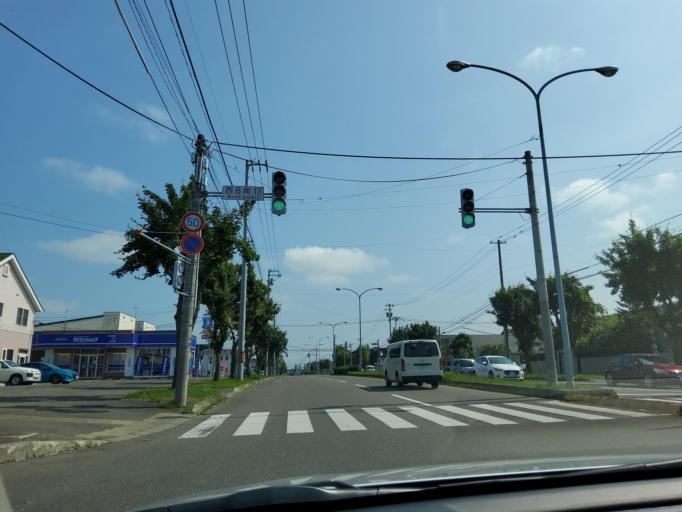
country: JP
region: Hokkaido
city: Obihiro
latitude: 42.9172
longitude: 143.1932
